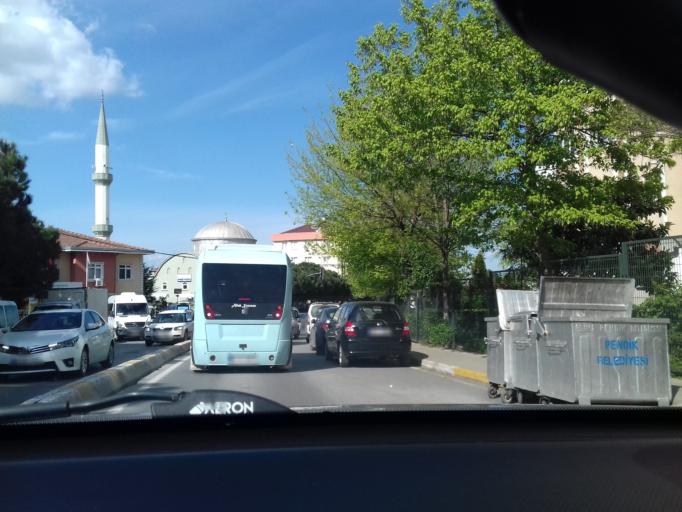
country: TR
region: Istanbul
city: Pendik
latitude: 40.9138
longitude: 29.2832
